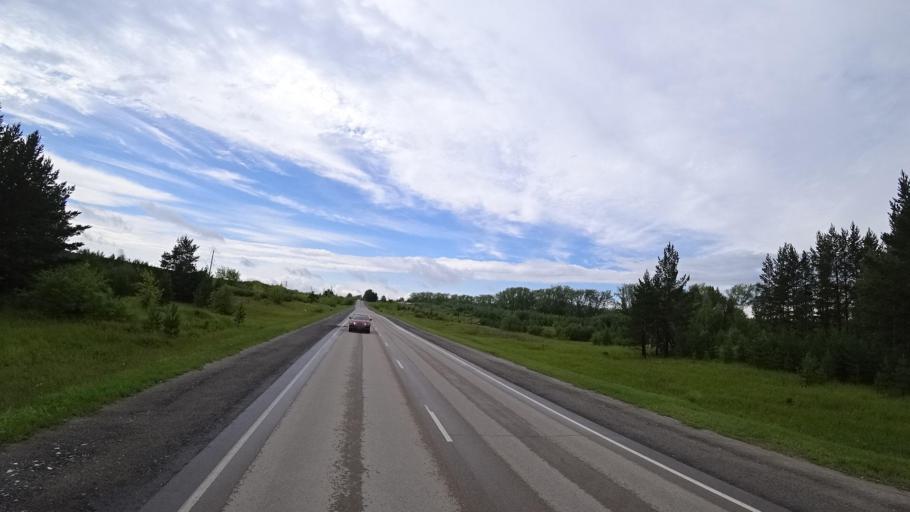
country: RU
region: Sverdlovsk
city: Kamyshlov
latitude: 56.8426
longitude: 62.7794
